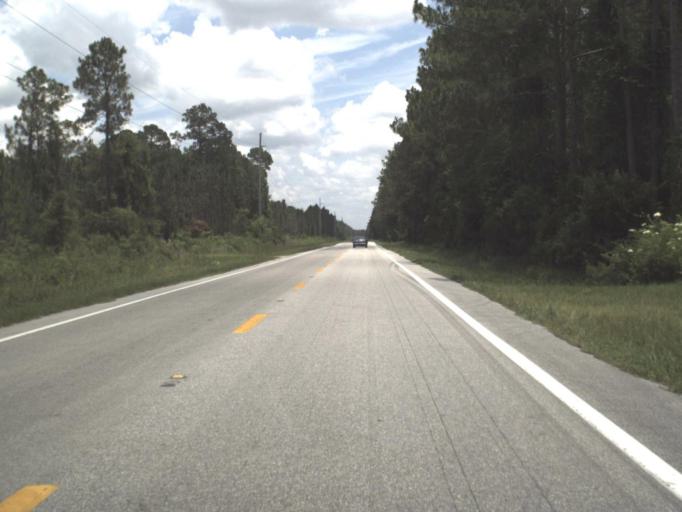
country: US
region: Florida
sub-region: Levy County
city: Bronson
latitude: 29.4249
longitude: -82.6702
